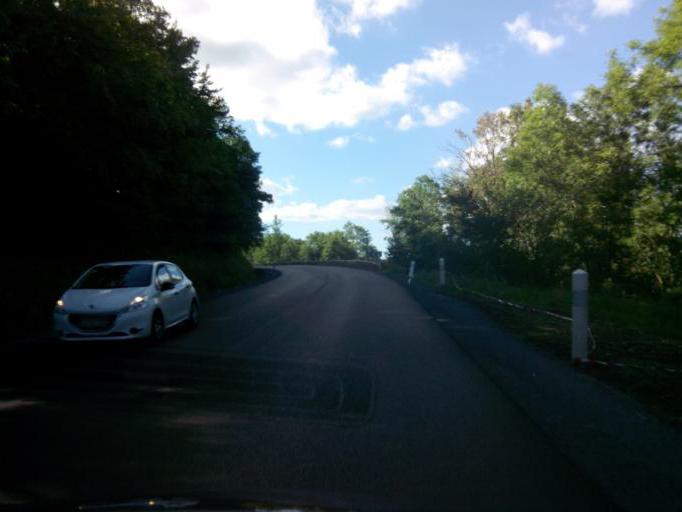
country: FR
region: Auvergne
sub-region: Departement de la Haute-Loire
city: Polignac
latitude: 45.0698
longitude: 3.8487
